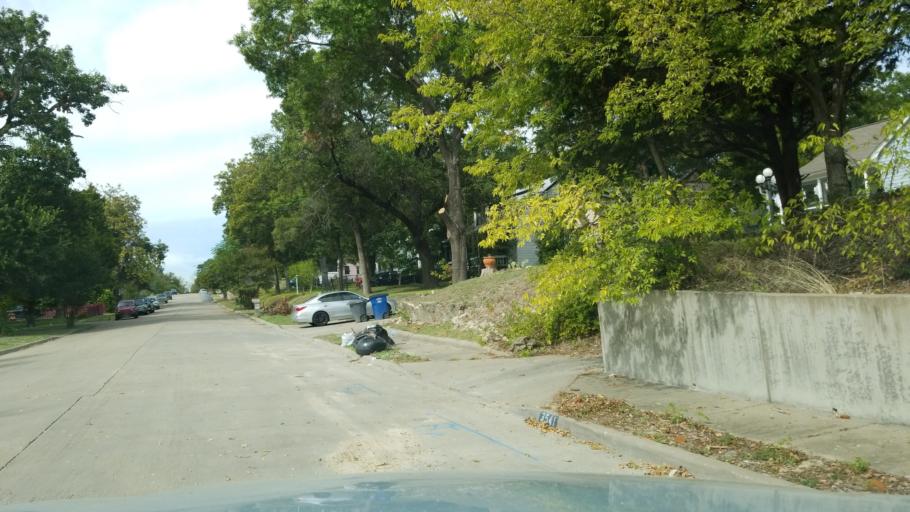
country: US
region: Texas
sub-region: Dallas County
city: Highland Park
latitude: 32.7894
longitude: -96.7336
